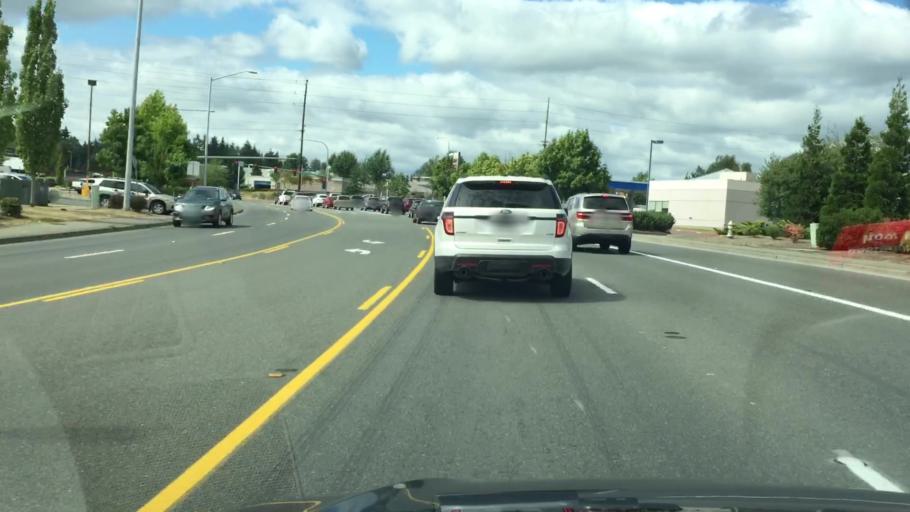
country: US
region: Washington
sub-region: Pierce County
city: Graham
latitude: 47.0984
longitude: -122.2915
